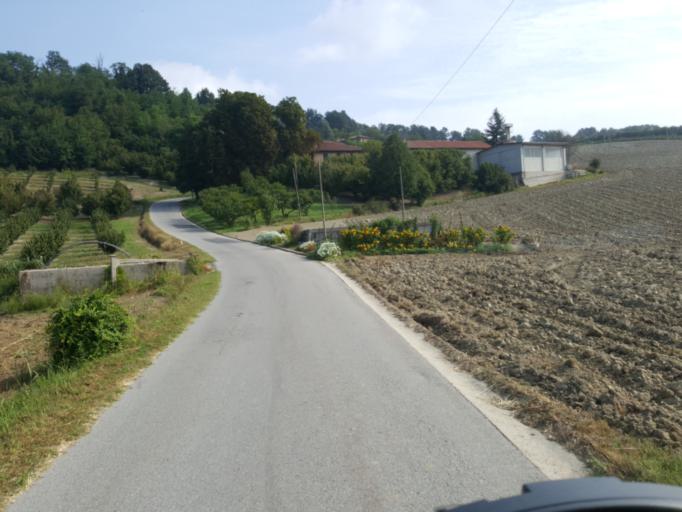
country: IT
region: Piedmont
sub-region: Provincia di Cuneo
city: Novello
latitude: 44.5934
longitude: 7.9009
